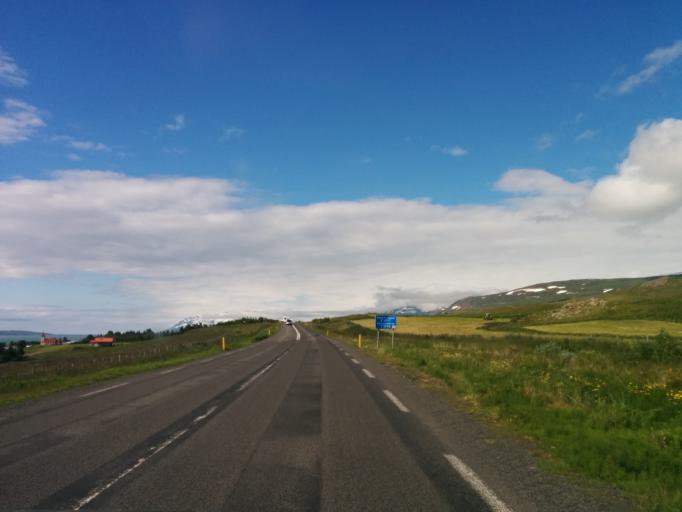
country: IS
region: Northeast
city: Akureyri
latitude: 65.7385
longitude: -18.0738
